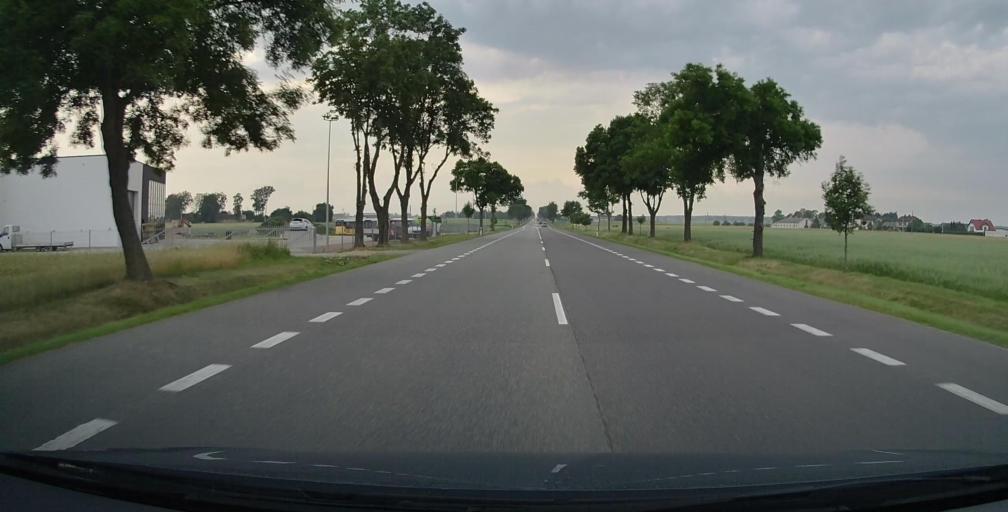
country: PL
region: Masovian Voivodeship
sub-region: Powiat siedlecki
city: Zbuczyn
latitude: 52.1027
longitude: 22.3998
